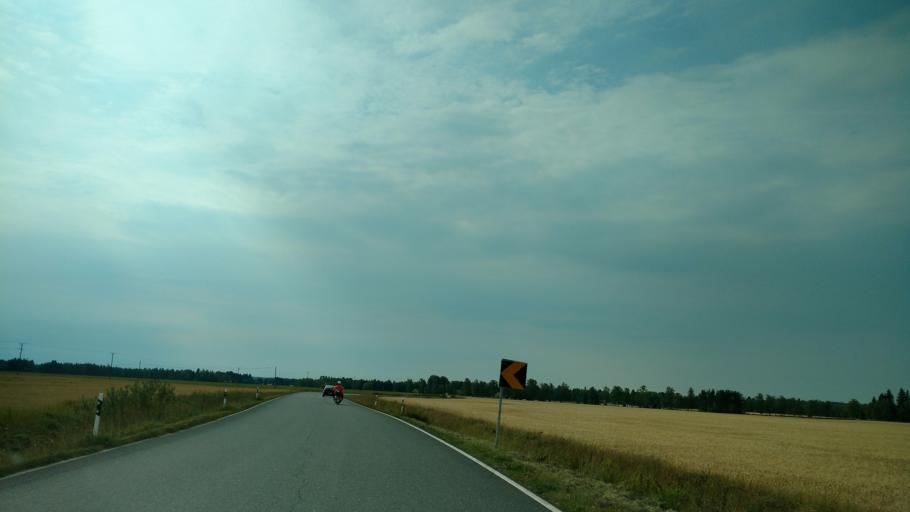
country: FI
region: Varsinais-Suomi
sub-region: Loimaa
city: Koski Tl
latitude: 60.6700
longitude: 23.1545
